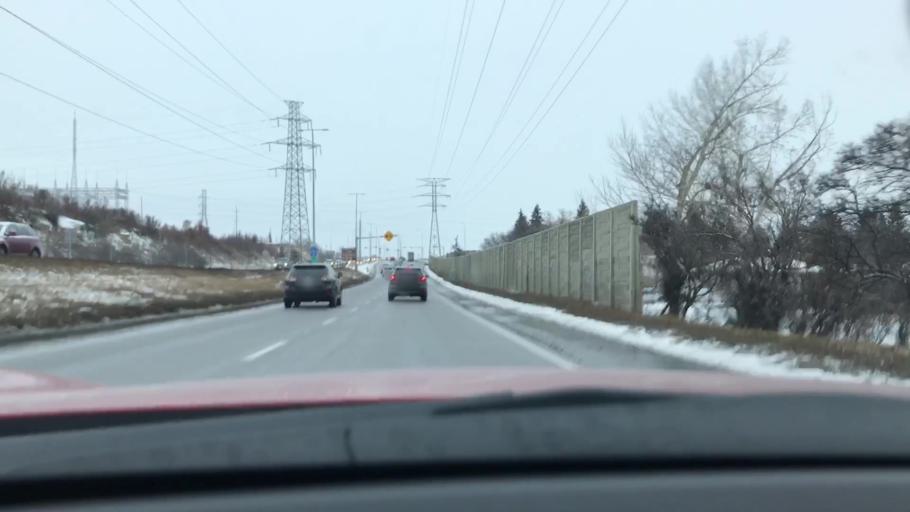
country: CA
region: Alberta
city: Calgary
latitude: 51.0488
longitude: -114.1642
